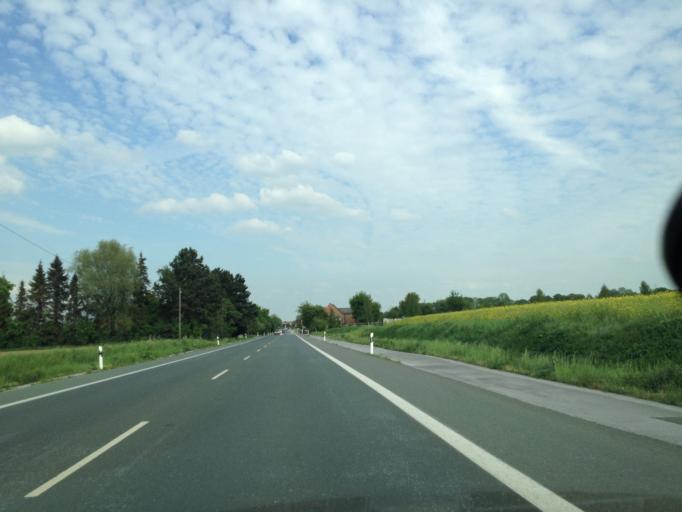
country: DE
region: North Rhine-Westphalia
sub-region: Regierungsbezirk Arnsberg
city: Soest
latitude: 51.5496
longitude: 8.0305
